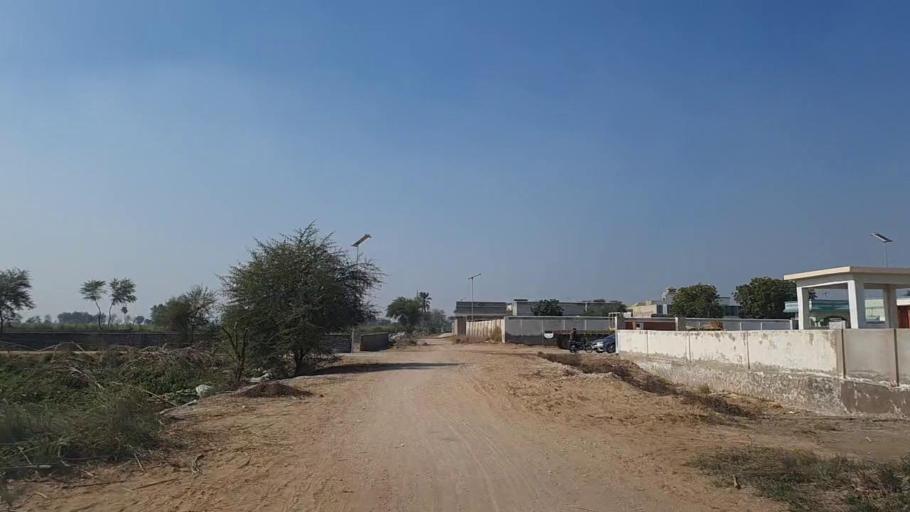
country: PK
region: Sindh
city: Daur
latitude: 26.5027
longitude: 68.3392
